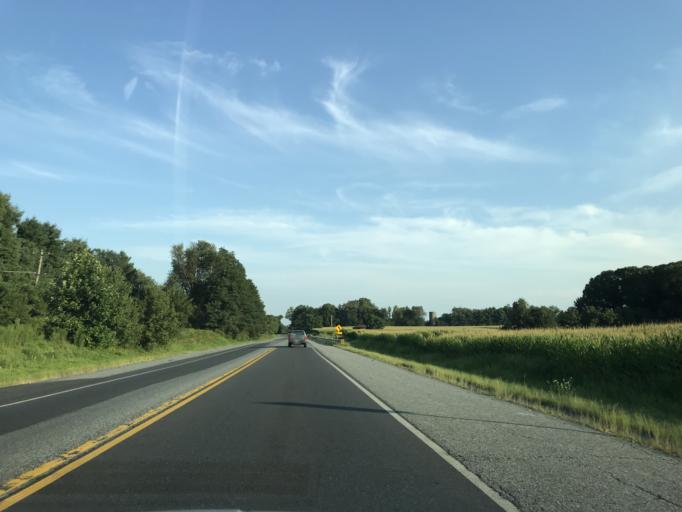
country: US
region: Maryland
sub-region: Cecil County
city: Rising Sun
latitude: 39.6870
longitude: -75.9721
